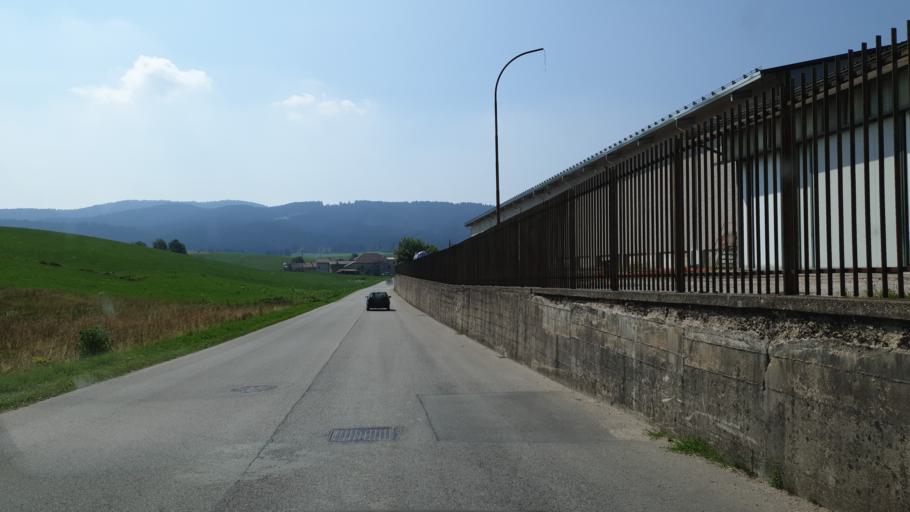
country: IT
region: Veneto
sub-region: Provincia di Vicenza
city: Asiago
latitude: 45.8679
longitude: 11.4975
